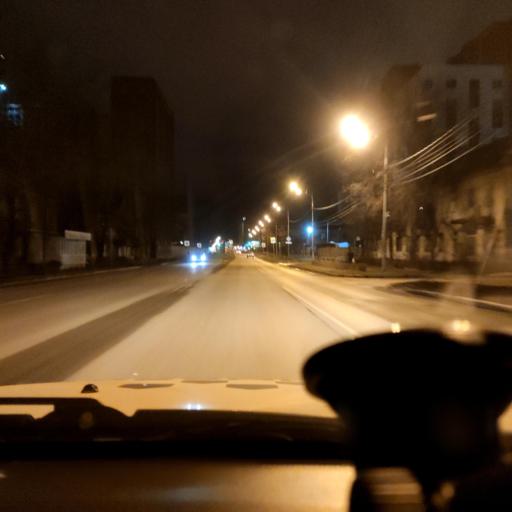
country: RU
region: Perm
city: Perm
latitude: 57.9810
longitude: 56.2161
